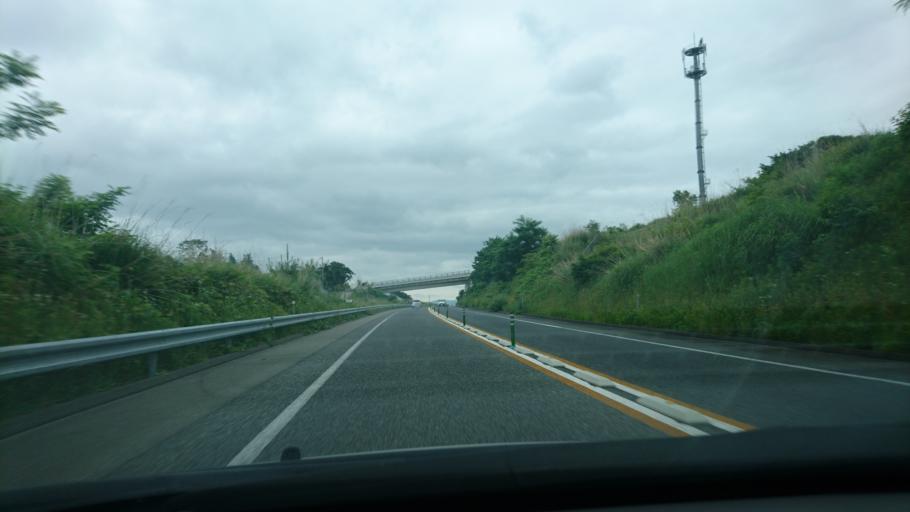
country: JP
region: Iwate
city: Ichinoseki
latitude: 38.7394
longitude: 141.1142
